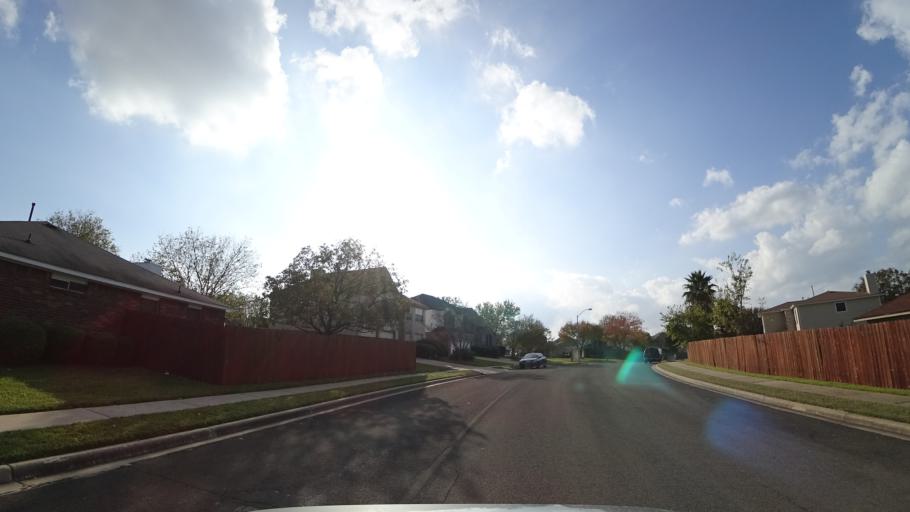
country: US
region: Texas
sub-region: Williamson County
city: Round Rock
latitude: 30.4903
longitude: -97.6608
